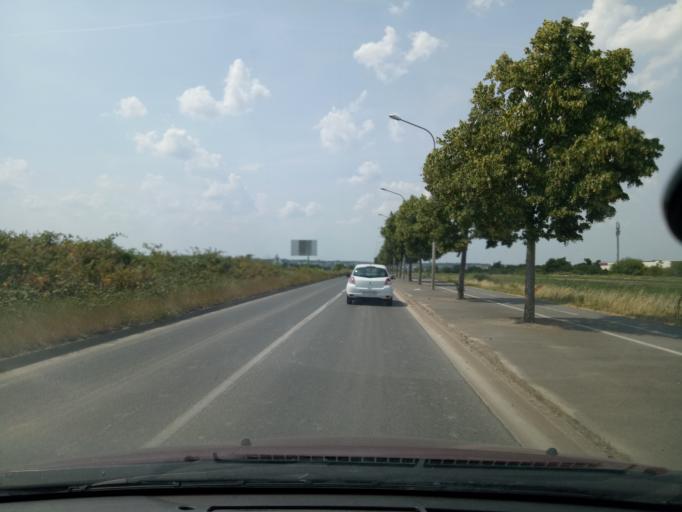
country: FR
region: Ile-de-France
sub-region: Departement des Yvelines
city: Montesson
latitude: 48.9230
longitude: 2.1554
